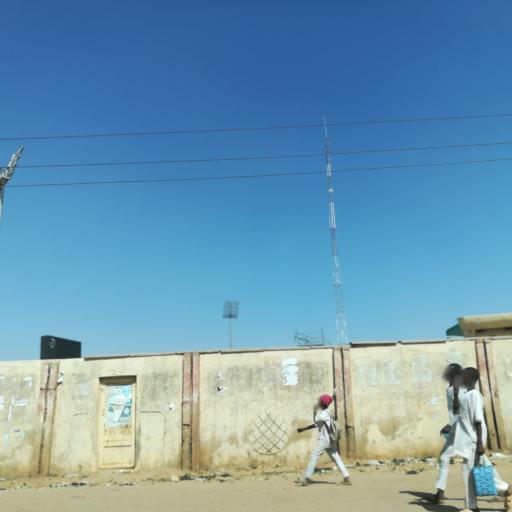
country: NG
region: Kano
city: Kano
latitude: 11.9994
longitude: 8.5280
